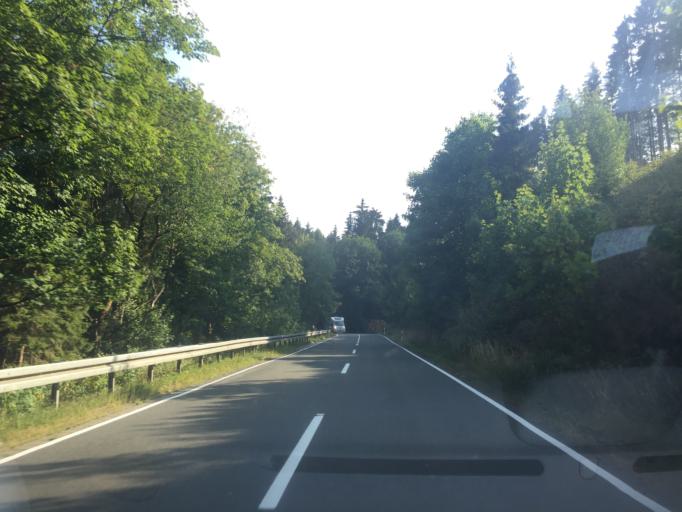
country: DE
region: Saxony-Anhalt
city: Darlingerode
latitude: 51.7862
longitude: 10.7389
